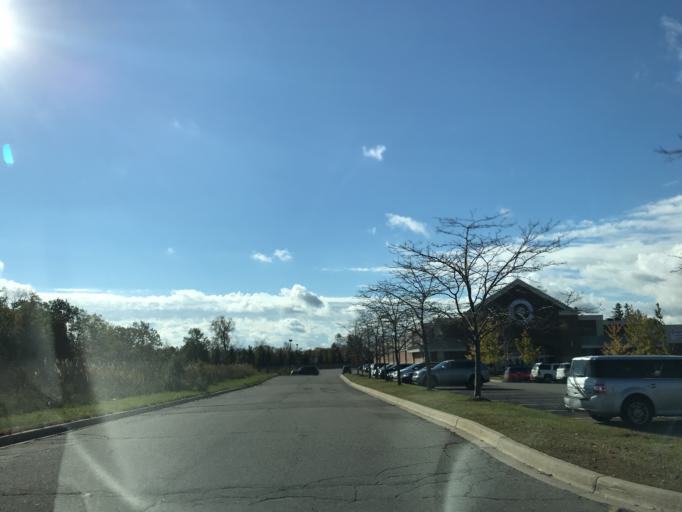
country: US
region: Michigan
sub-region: Oakland County
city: Wixom
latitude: 42.4893
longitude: -83.5333
